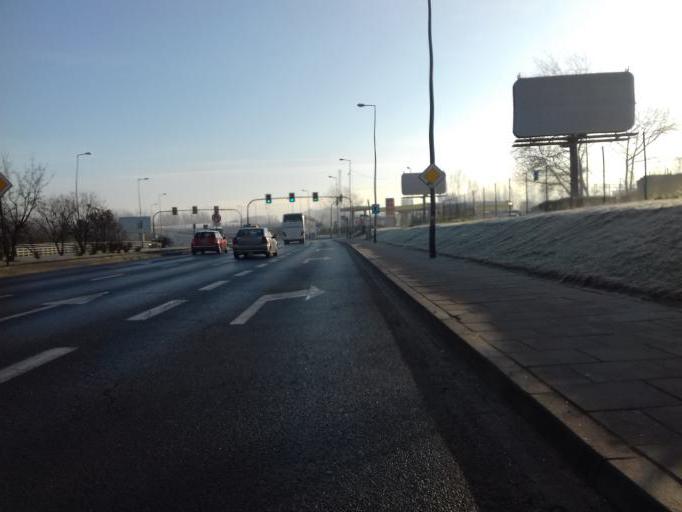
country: PL
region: Lesser Poland Voivodeship
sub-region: Krakow
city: Krakow
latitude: 50.0285
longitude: 19.9396
